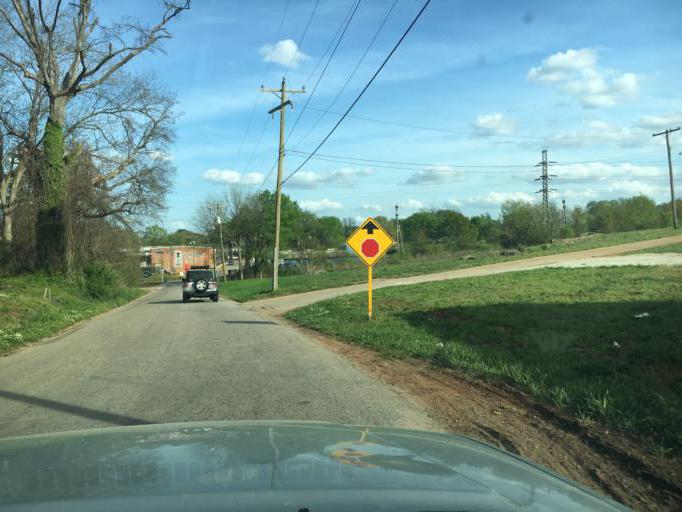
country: US
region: South Carolina
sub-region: Greenville County
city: Sans Souci
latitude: 34.8670
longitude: -82.4186
